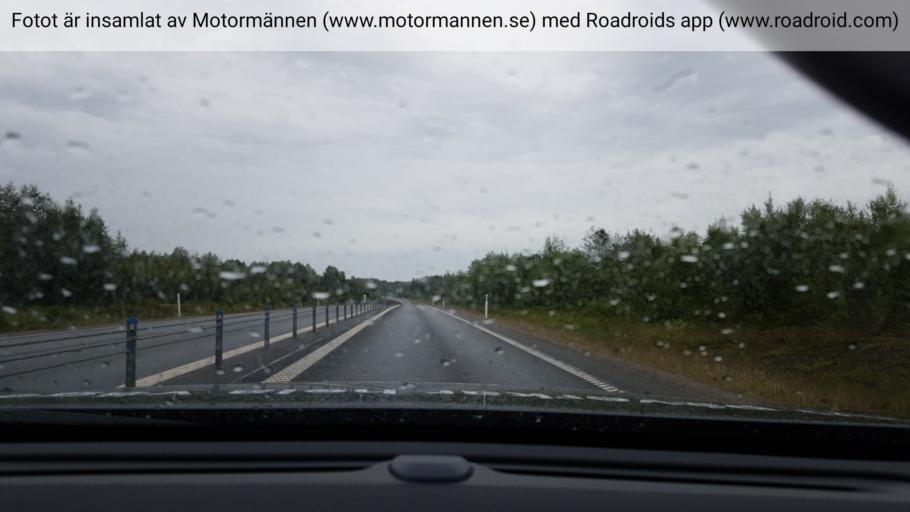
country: SE
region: Vaesterbotten
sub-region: Vannas Kommun
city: Vannasby
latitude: 63.8990
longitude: 19.9068
